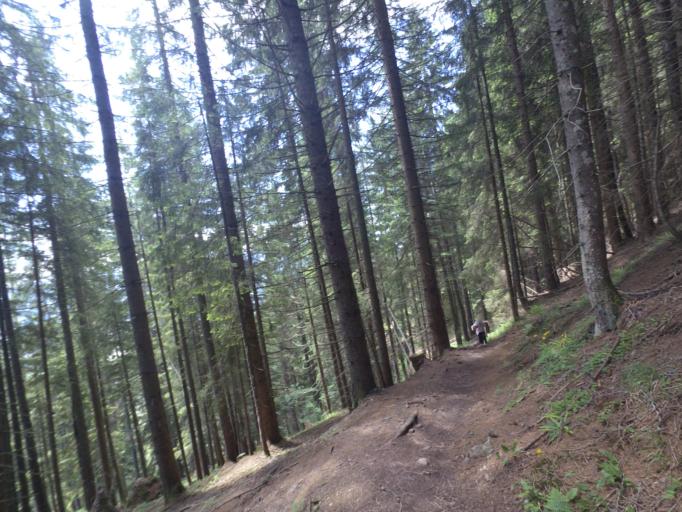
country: AT
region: Salzburg
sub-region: Politischer Bezirk Zell am See
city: Leogang
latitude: 47.4607
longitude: 12.7723
